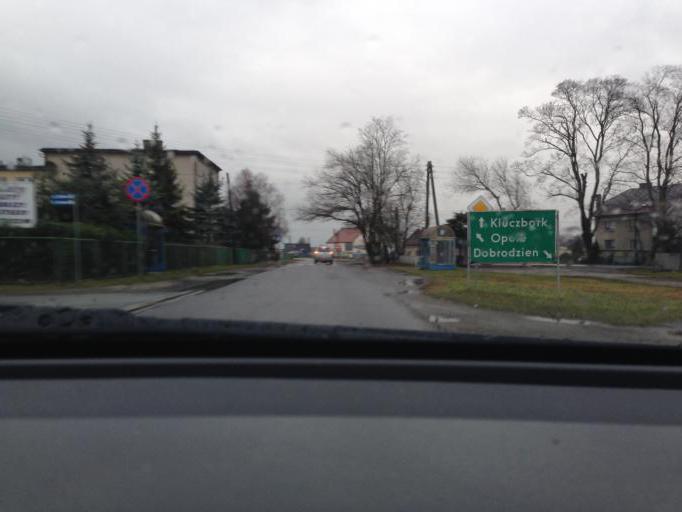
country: PL
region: Opole Voivodeship
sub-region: Powiat opolski
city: Wegry
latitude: 50.7305
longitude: 18.0456
